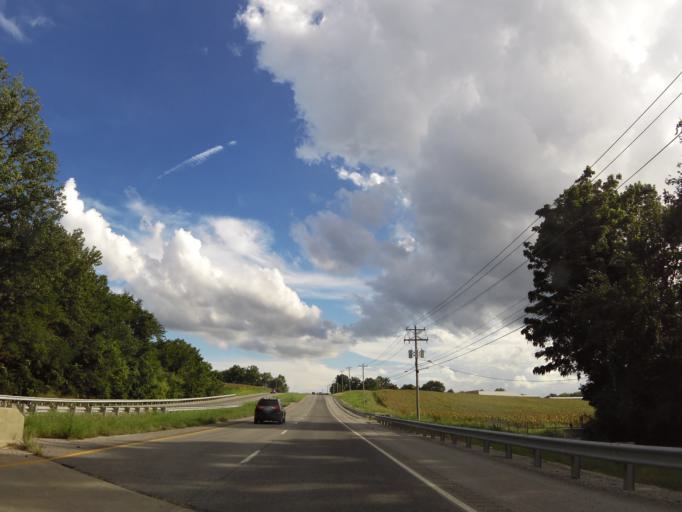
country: US
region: Kentucky
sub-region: Christian County
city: Hopkinsville
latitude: 36.7945
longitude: -87.4734
